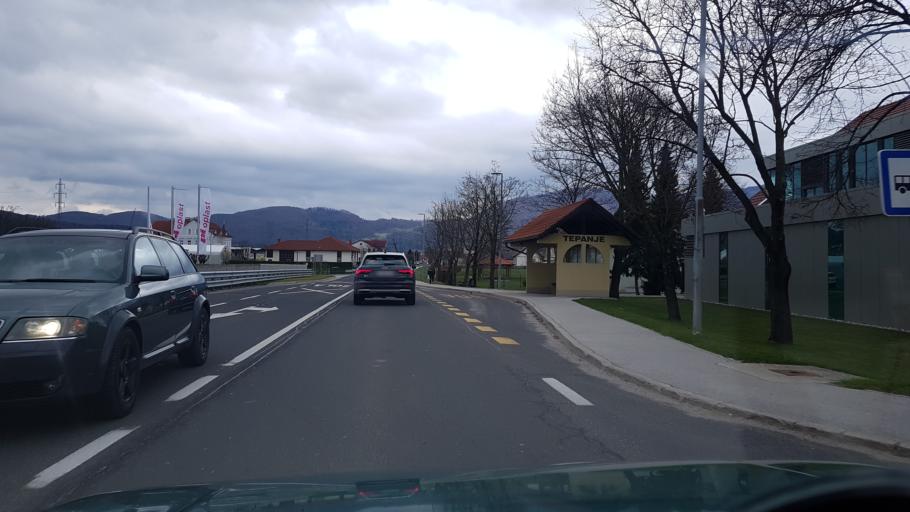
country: SI
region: Oplotnica
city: Oplotnica
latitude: 46.3465
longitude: 15.4756
